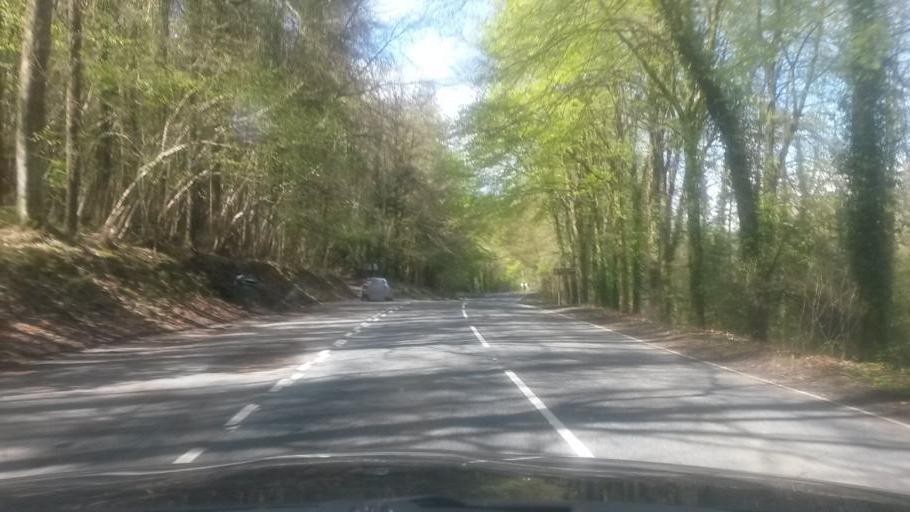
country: GB
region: Northern Ireland
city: Irvinestown
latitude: 54.4142
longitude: -7.7277
